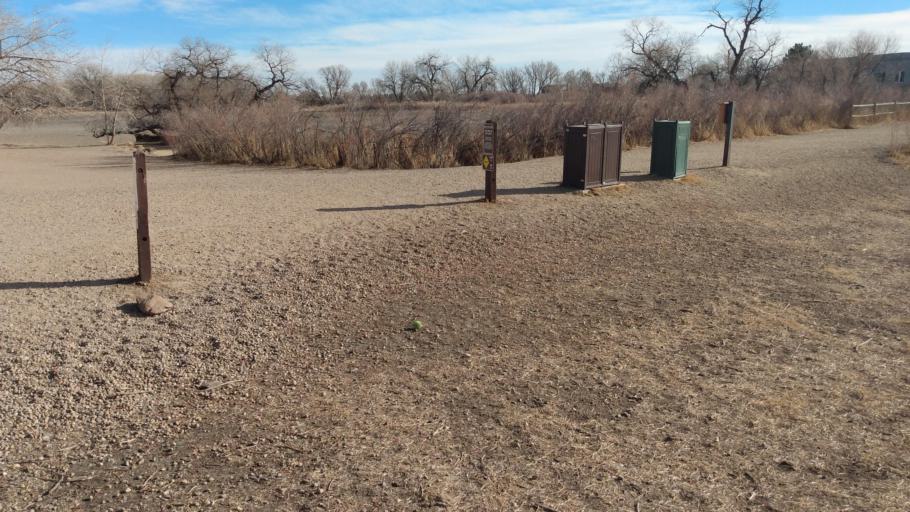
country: US
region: Colorado
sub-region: Boulder County
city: Gunbarrel
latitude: 40.0619
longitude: -105.2039
